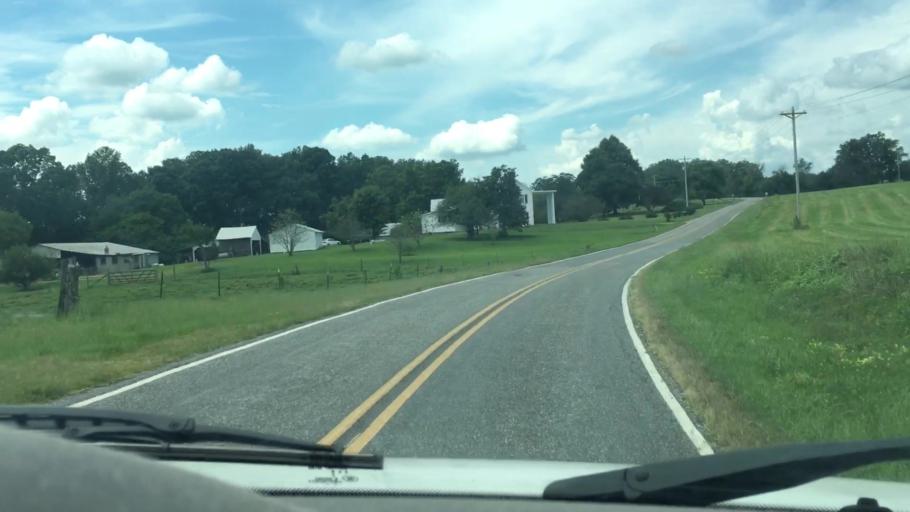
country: US
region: North Carolina
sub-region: Iredell County
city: Mooresville
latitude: 35.6625
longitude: -80.8151
